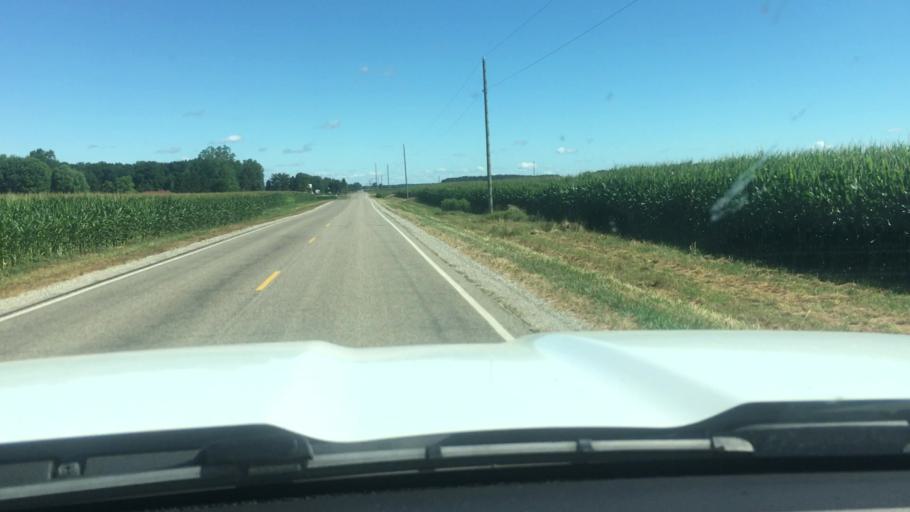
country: US
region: Michigan
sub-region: Montcalm County
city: Carson City
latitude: 43.1866
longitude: -84.7780
